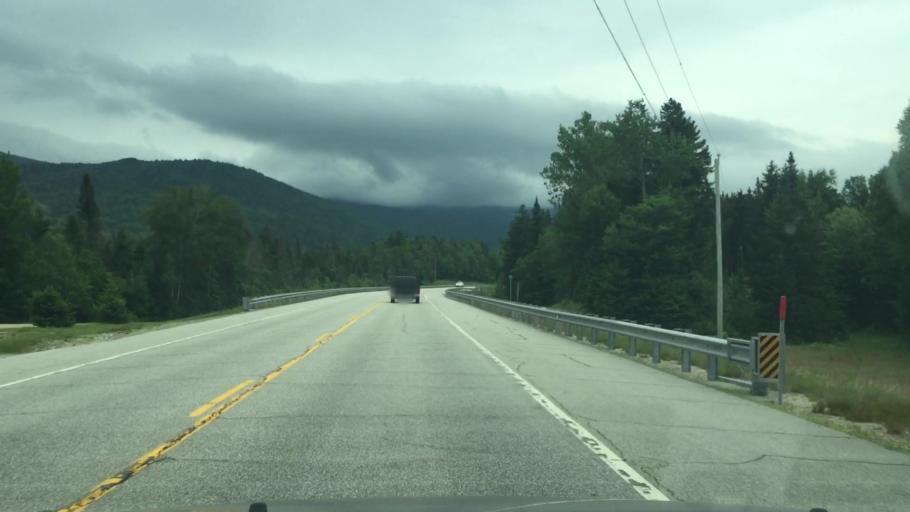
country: US
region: New Hampshire
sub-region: Coos County
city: Jefferson
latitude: 44.2393
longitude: -71.4256
